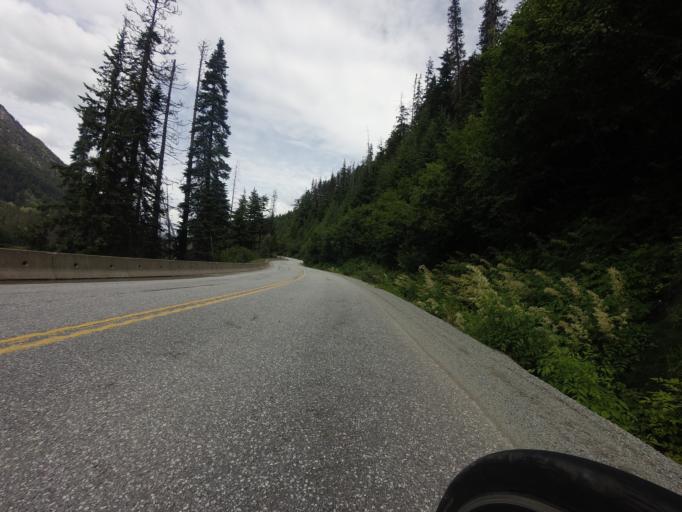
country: CA
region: British Columbia
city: Lillooet
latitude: 50.4133
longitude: -122.2836
